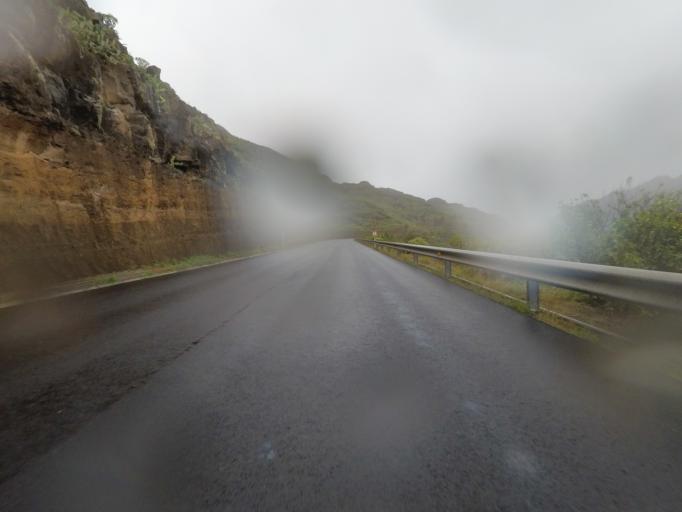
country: ES
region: Canary Islands
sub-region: Provincia de Santa Cruz de Tenerife
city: Alajero
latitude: 28.0665
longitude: -17.2053
